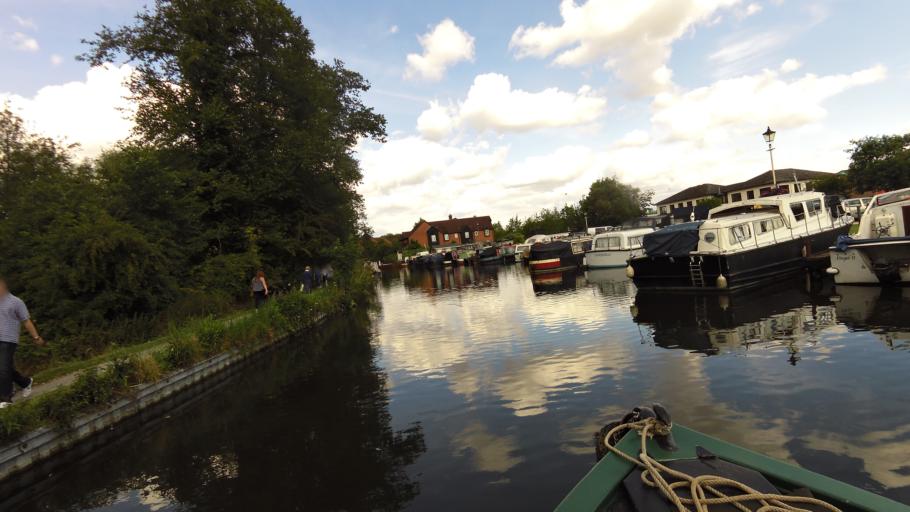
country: GB
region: England
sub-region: West Berkshire
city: Newbury
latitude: 51.4013
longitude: -1.3173
